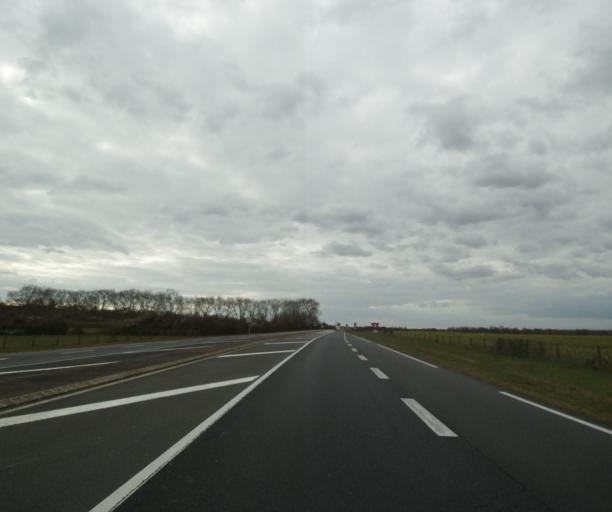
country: FR
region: Auvergne
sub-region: Departement de l'Allier
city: Toulon-sur-Allier
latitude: 46.4923
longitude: 3.3644
